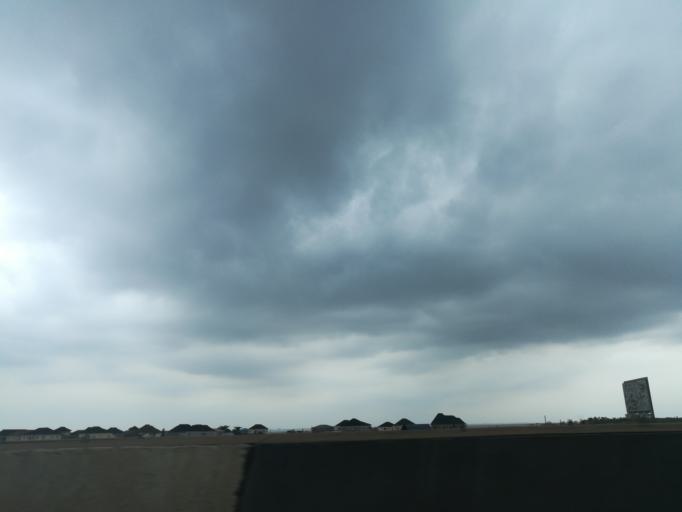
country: NG
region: Lagos
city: Somolu
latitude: 6.5342
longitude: 3.4009
